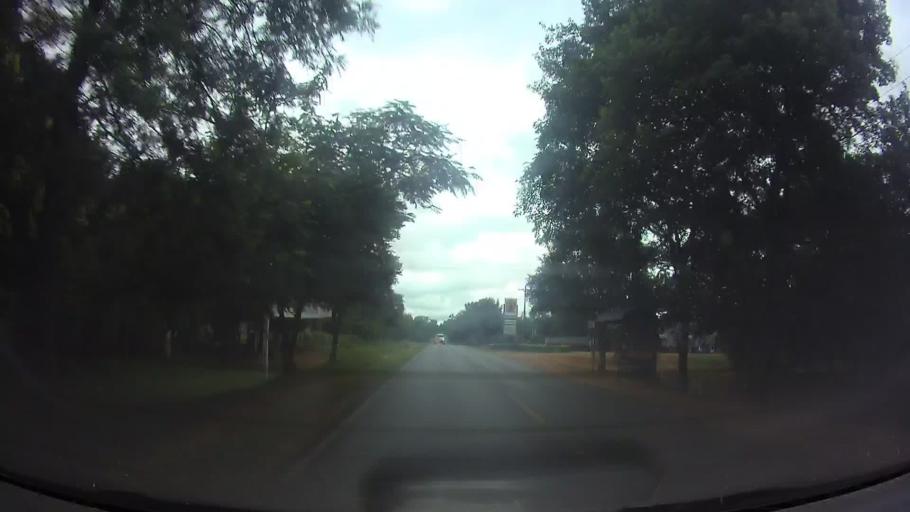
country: PY
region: Central
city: Guarambare
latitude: -25.5434
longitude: -57.4997
